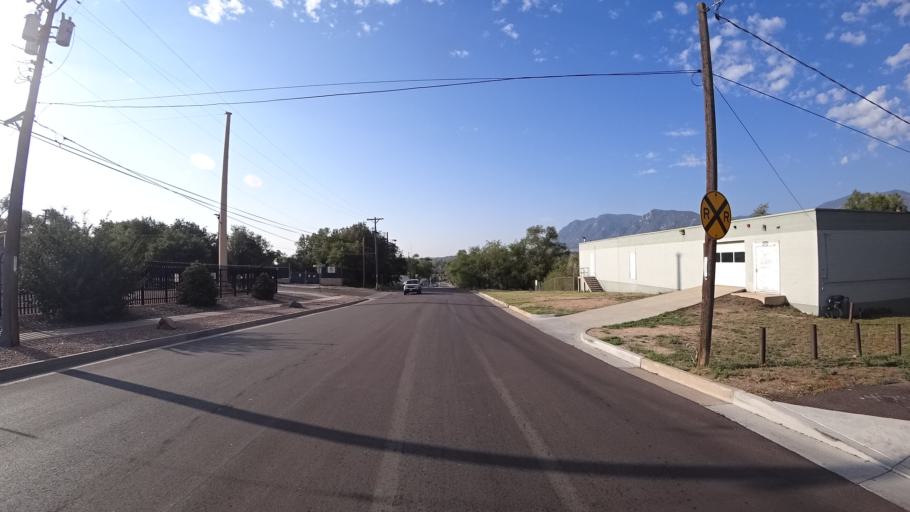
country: US
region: Colorado
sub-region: El Paso County
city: Colorado Springs
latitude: 38.8193
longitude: -104.8154
